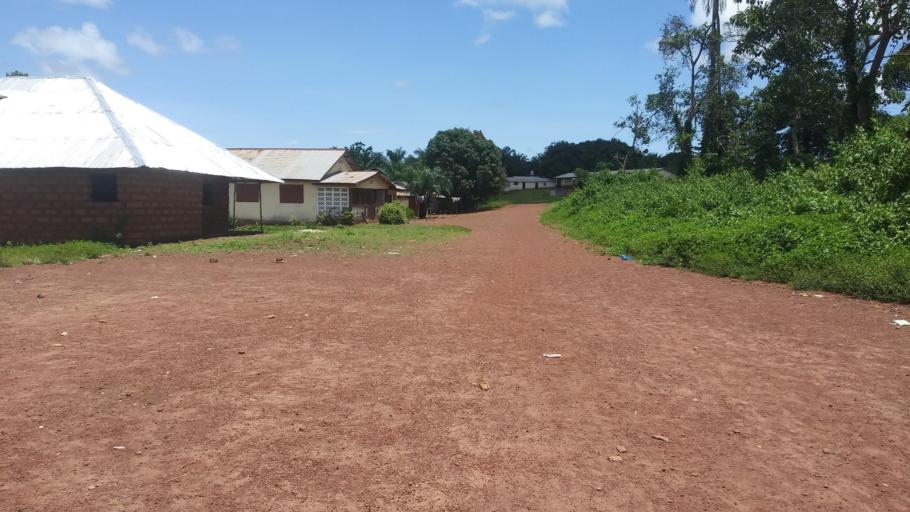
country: SL
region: Northern Province
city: Binkolo
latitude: 8.9017
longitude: -11.9892
